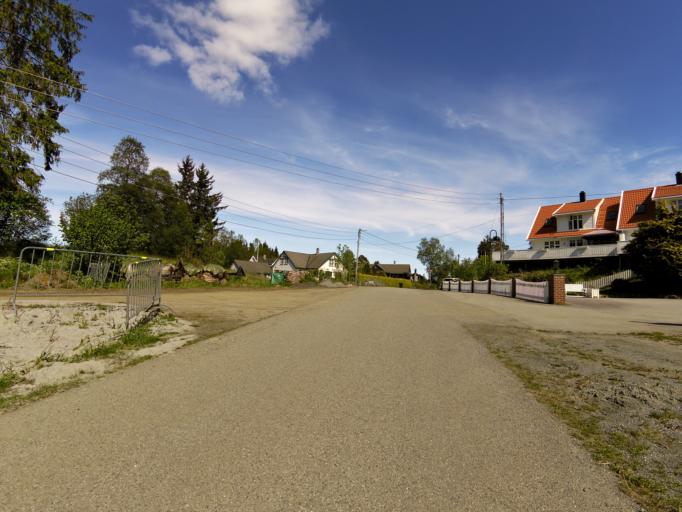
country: NO
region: Hordaland
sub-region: Stord
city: Leirvik
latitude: 59.7877
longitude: 5.4907
